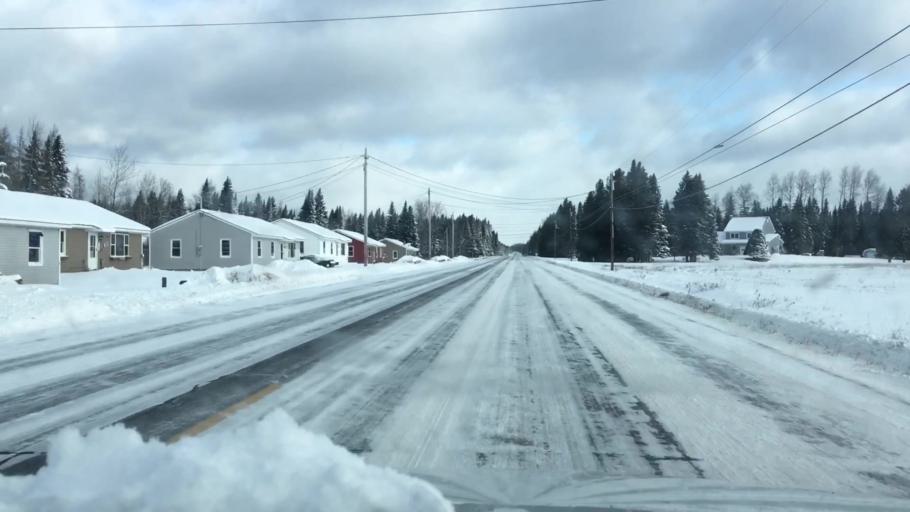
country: US
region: Maine
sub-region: Aroostook County
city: Madawaska
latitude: 47.0114
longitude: -68.0193
